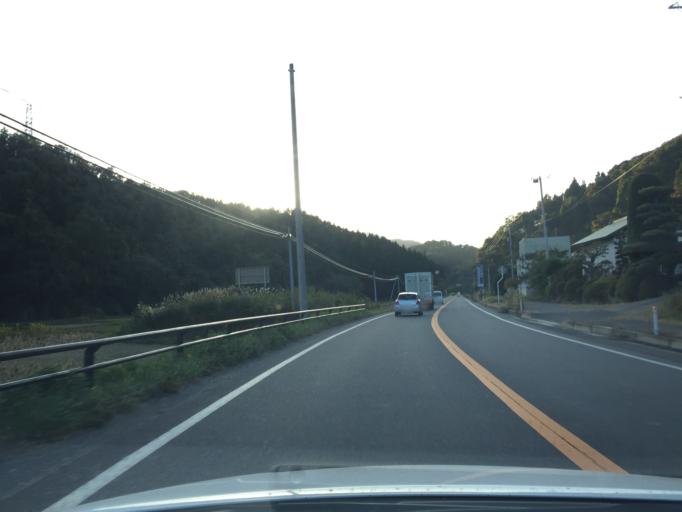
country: JP
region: Fukushima
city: Sukagawa
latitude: 37.3012
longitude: 140.5040
